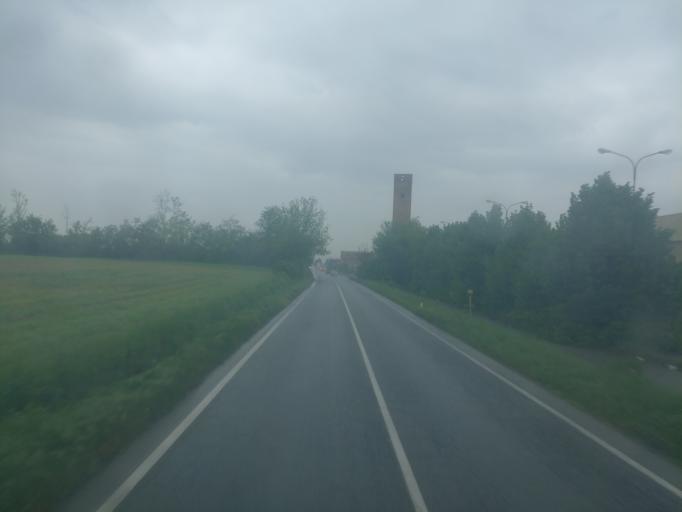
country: IT
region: Piedmont
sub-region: Provincia di Torino
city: Carignano
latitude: 44.8871
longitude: 7.6680
